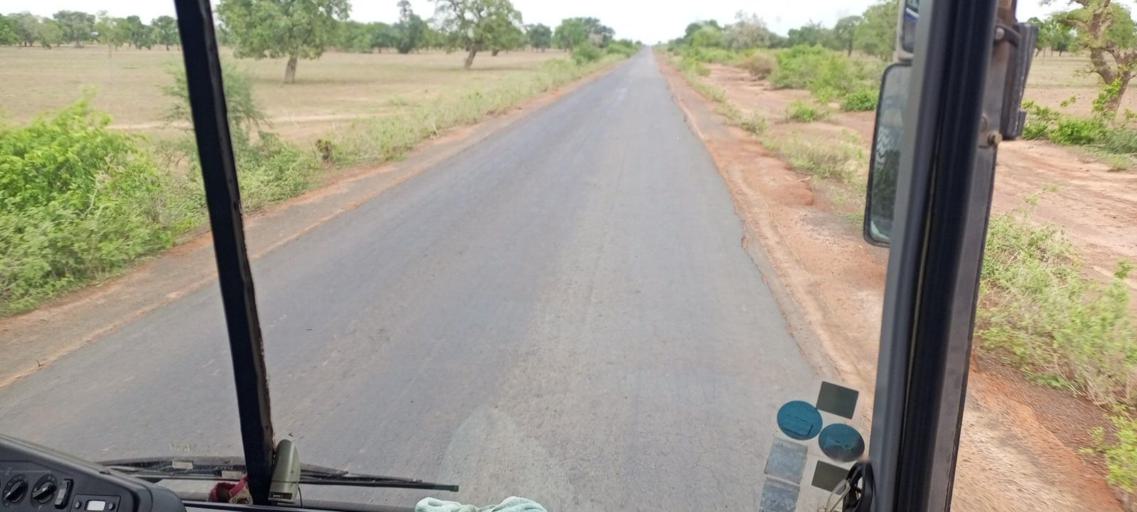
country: ML
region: Segou
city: Bla
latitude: 12.7288
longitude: -5.7253
